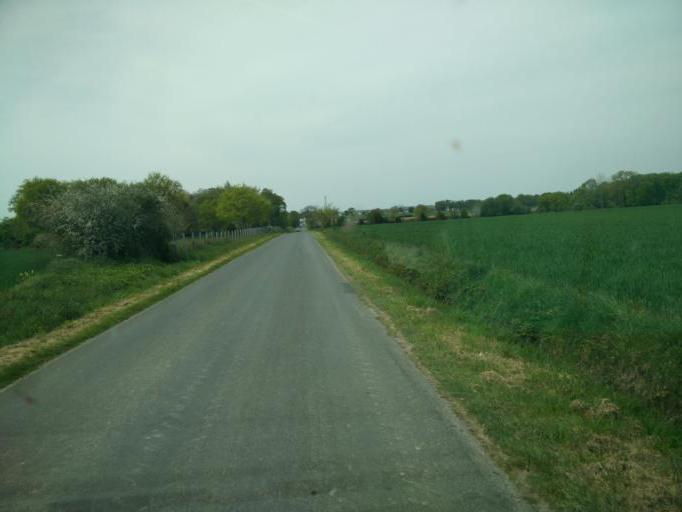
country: FR
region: Brittany
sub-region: Departement des Cotes-d'Armor
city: Matignon
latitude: 48.5909
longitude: -2.2680
